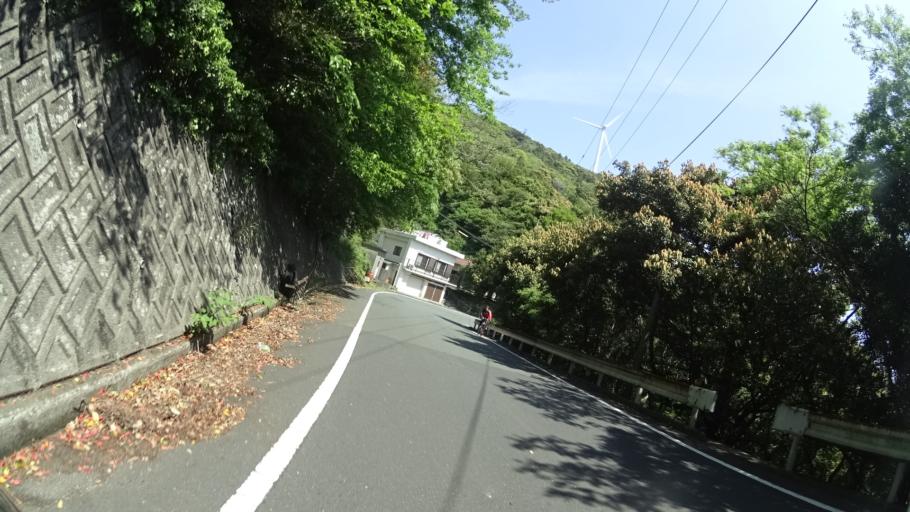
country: JP
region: Ehime
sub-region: Nishiuwa-gun
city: Ikata-cho
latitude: 33.3829
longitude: 132.0851
